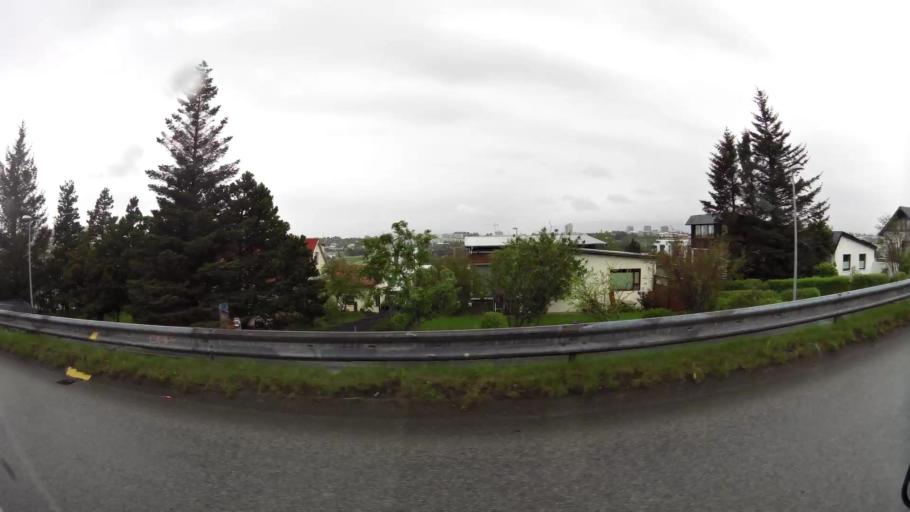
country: IS
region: Capital Region
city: Kopavogur
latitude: 64.1122
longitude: -21.8962
